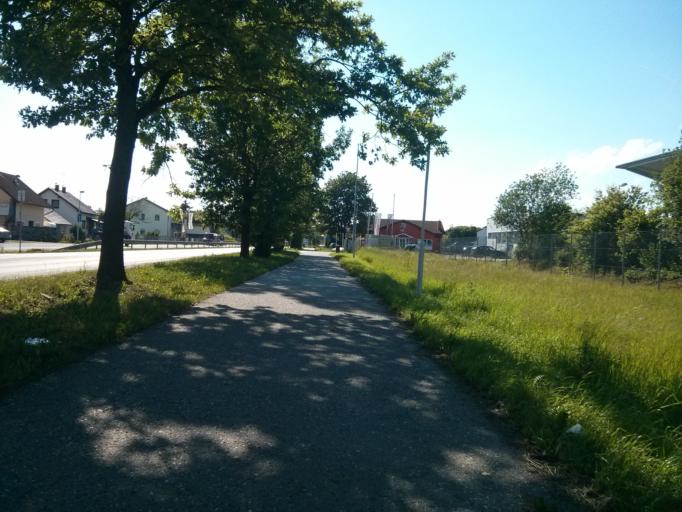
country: DE
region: Bavaria
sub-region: Lower Bavaria
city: Deggendorf
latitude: 48.8235
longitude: 12.9418
